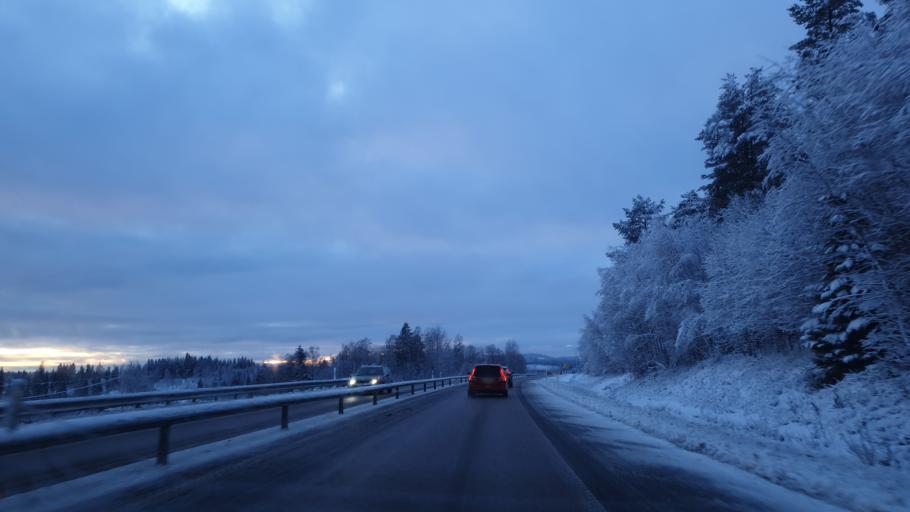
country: SE
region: Vaesternorrland
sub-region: OErnskoeldsviks Kommun
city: Ornskoldsvik
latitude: 63.3023
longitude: 18.9035
